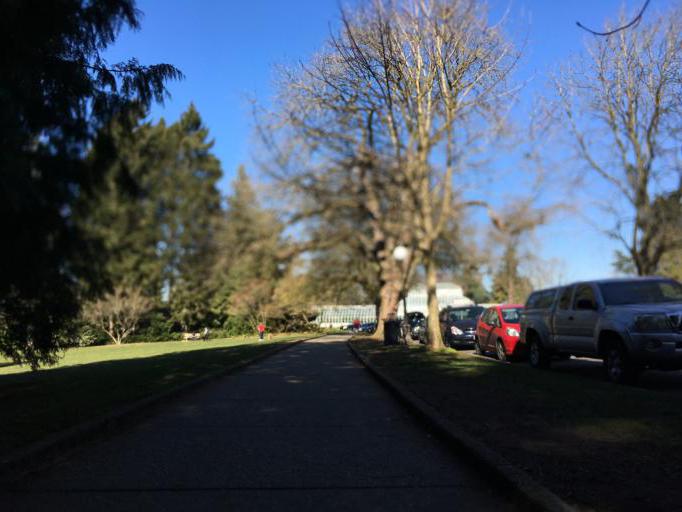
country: US
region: Washington
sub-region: King County
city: Seattle
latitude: 47.6309
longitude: -122.3157
